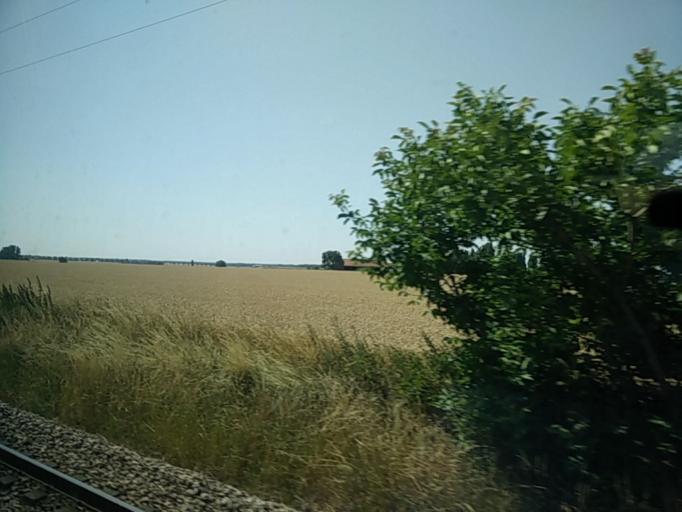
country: FR
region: Ile-de-France
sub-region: Departement de Seine-et-Marne
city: Bailly-Carrois
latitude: 48.5740
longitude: 2.9955
